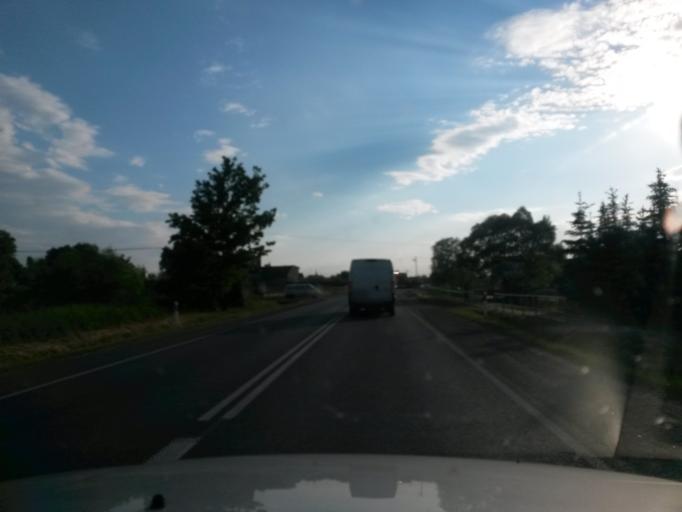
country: PL
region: Lodz Voivodeship
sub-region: Powiat belchatowski
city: Kluki
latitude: 51.3418
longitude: 19.2412
